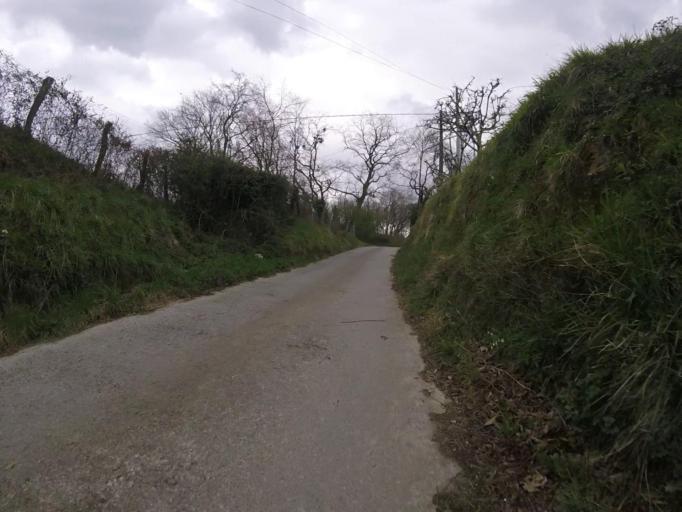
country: ES
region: Basque Country
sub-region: Provincia de Guipuzcoa
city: Errenteria
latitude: 43.2802
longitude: -1.8625
